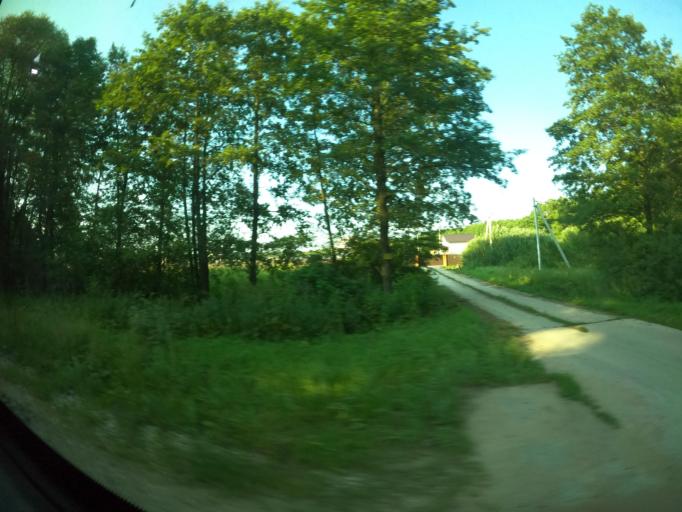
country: RU
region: Moskovskaya
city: Obolensk
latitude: 54.9419
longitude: 37.2408
